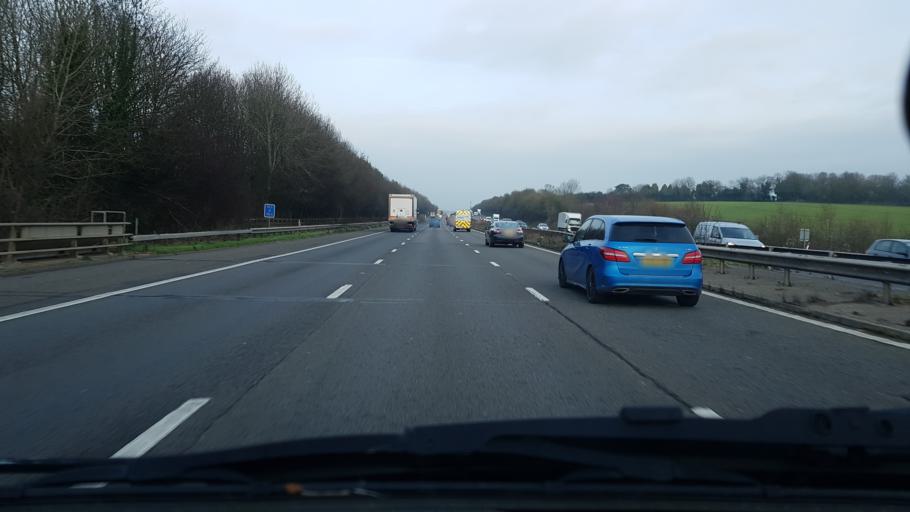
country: GB
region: England
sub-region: Hampshire
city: Basingstoke
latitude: 51.2379
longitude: -1.1095
